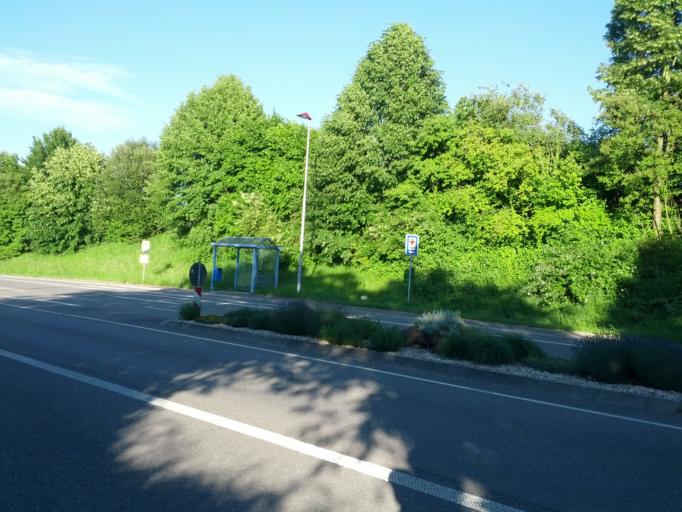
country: DE
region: Baden-Wuerttemberg
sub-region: Freiburg Region
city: Pfaffenweiler
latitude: 47.9438
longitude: 7.7360
